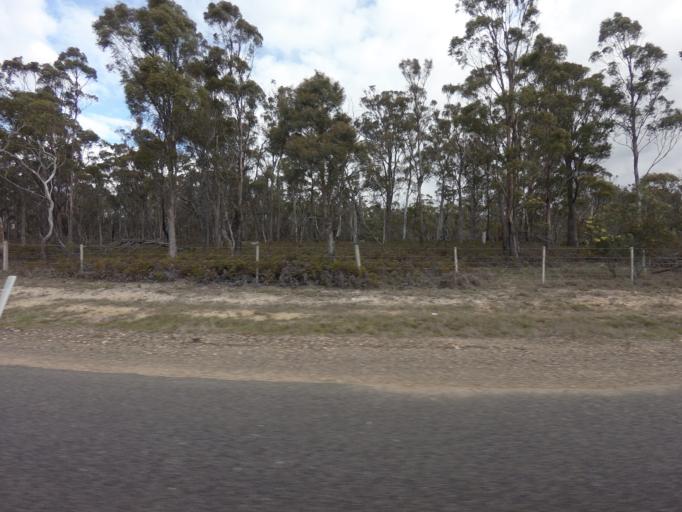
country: AU
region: Tasmania
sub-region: Northern Midlands
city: Longford
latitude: -41.8015
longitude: 147.1373
